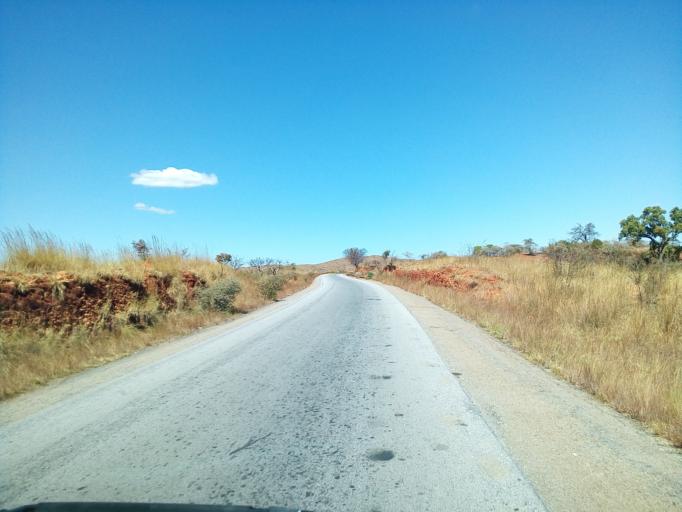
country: MG
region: Betsiboka
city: Maevatanana
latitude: -17.1347
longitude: 46.8106
